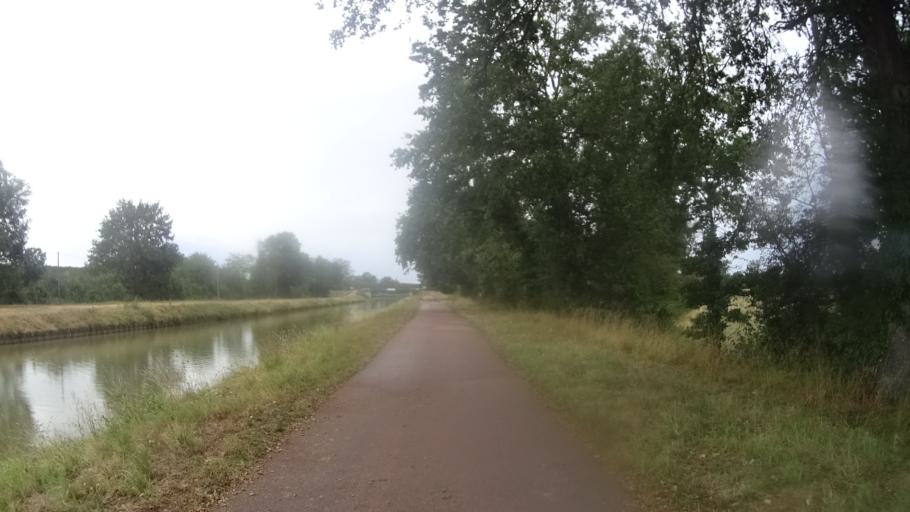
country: FR
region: Bourgogne
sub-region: Departement de la Nievre
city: Imphy
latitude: 46.8716
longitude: 3.2731
